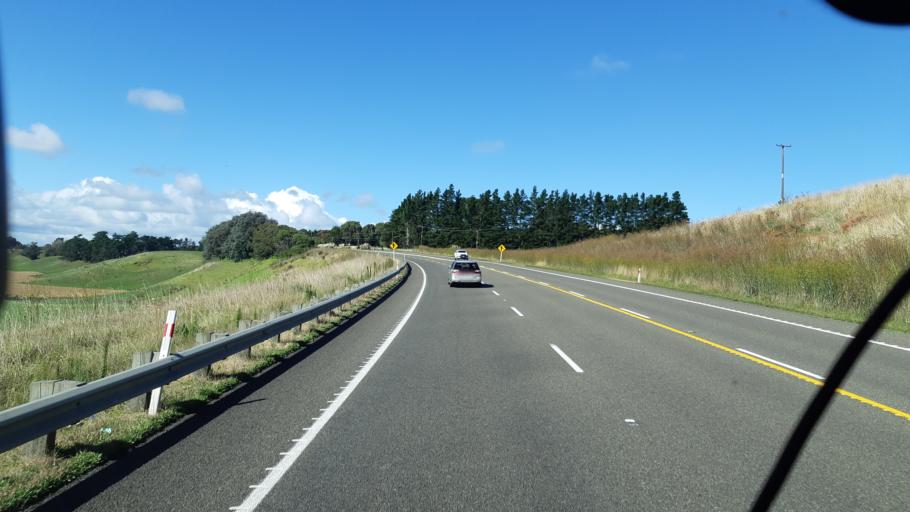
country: NZ
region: Manawatu-Wanganui
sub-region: Wanganui District
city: Wanganui
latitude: -39.9713
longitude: 175.1101
